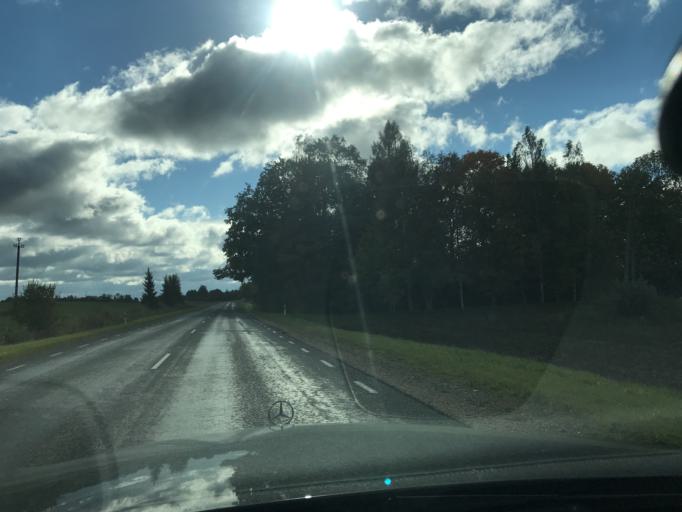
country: EE
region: Vorumaa
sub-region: Antsla vald
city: Vana-Antsla
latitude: 57.9637
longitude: 26.2692
